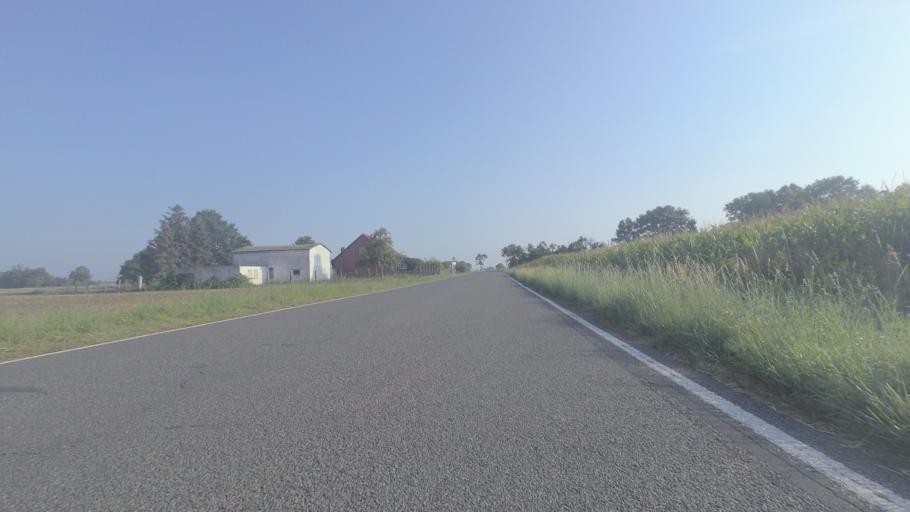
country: DE
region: Brandenburg
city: Heiligengrabe
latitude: 53.2675
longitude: 12.3375
